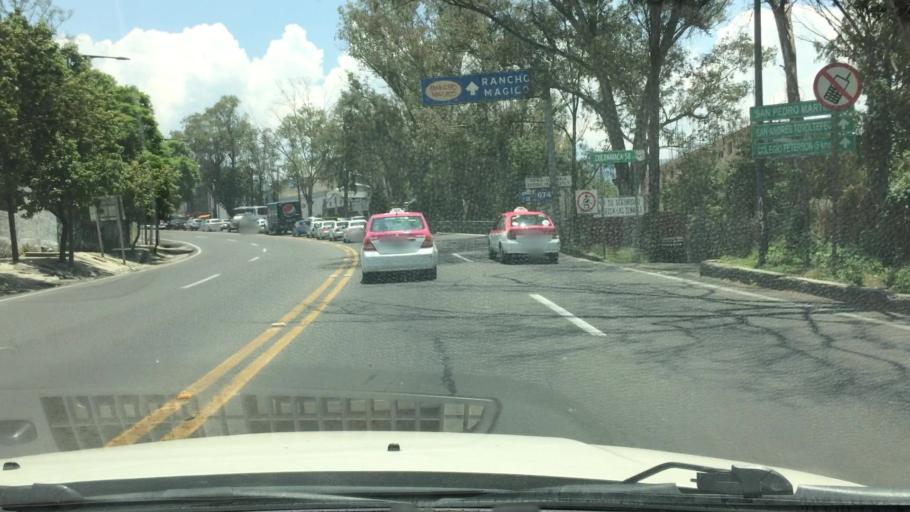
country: MX
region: Mexico City
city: Tlalpan
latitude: 19.2707
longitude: -99.1700
